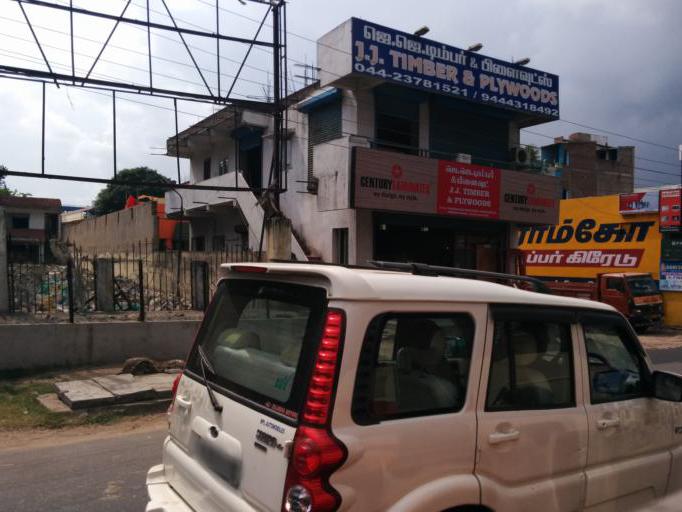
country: IN
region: Tamil Nadu
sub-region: Thiruvallur
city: Porur
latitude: 13.0641
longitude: 80.1697
